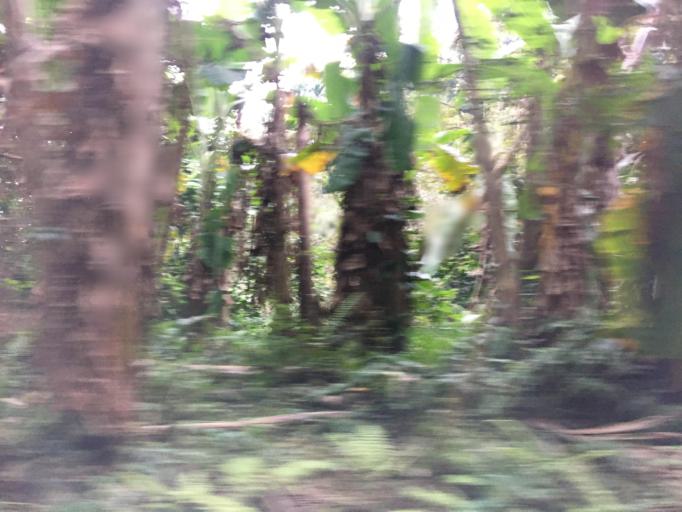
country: TW
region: Taiwan
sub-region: Chiayi
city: Jiayi Shi
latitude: 23.5386
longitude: 120.6055
